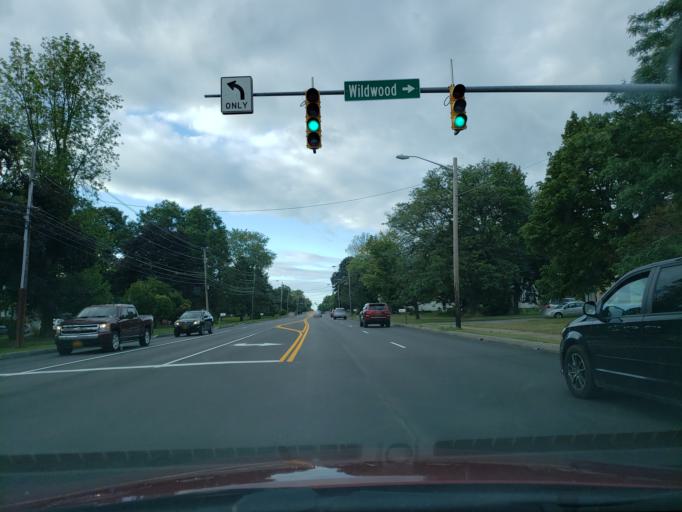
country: US
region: New York
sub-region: Monroe County
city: Greece
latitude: 43.2281
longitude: -77.6590
